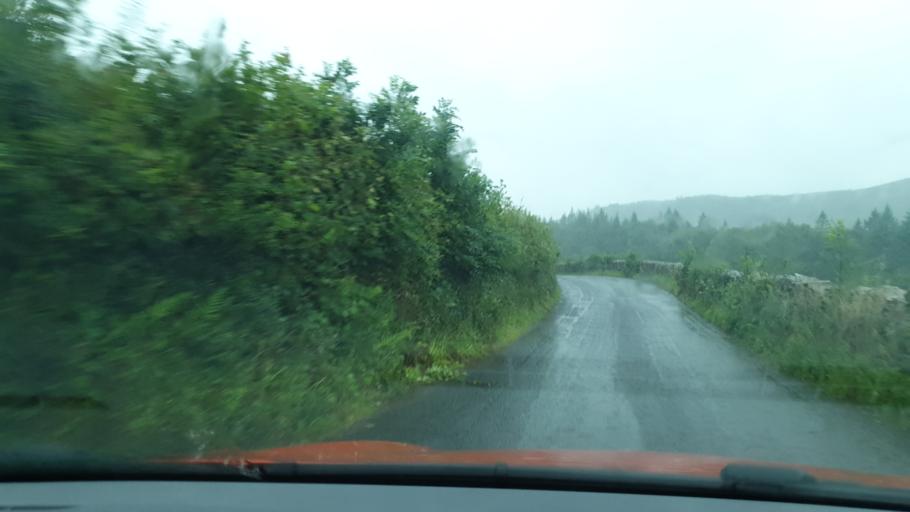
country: GB
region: England
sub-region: Cumbria
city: Millom
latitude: 54.2929
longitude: -3.2294
